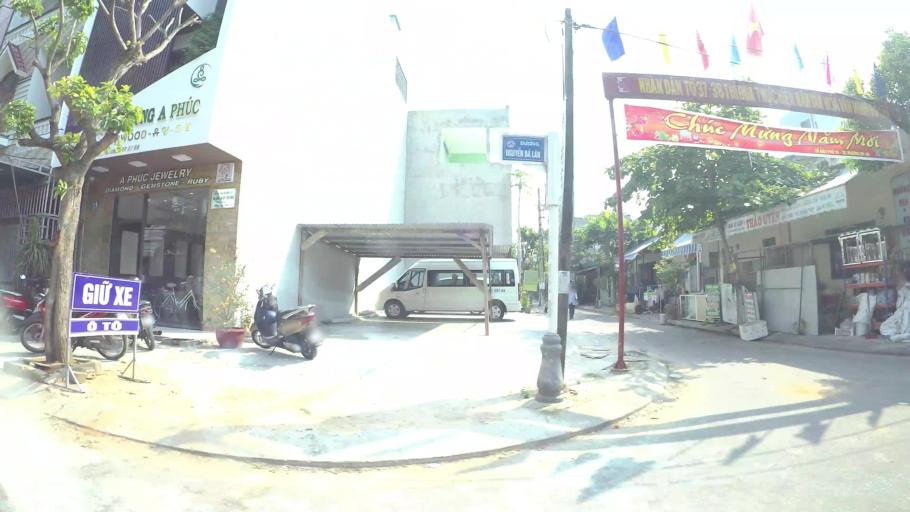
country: VN
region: Da Nang
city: Son Tra
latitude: 16.0409
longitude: 108.2427
